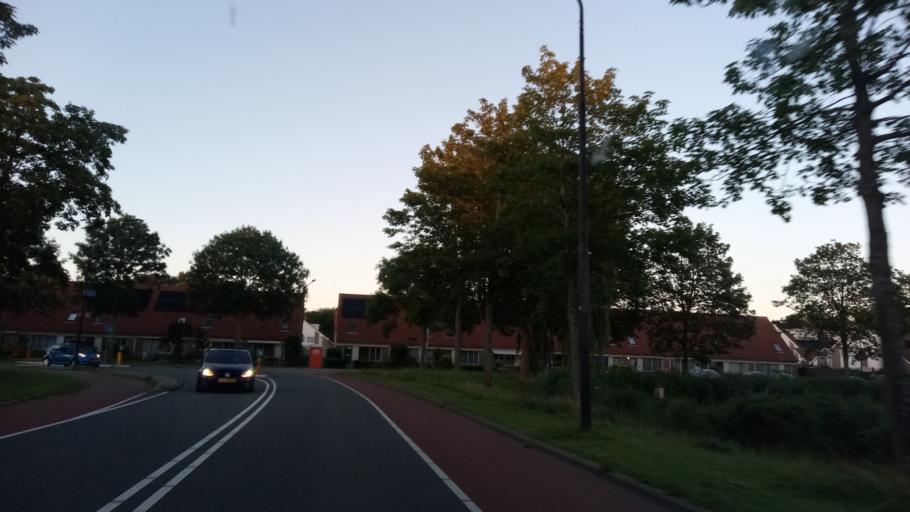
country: NL
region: North Holland
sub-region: Gemeente Langedijk
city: Broek op Langedijk
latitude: 52.6580
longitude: 4.8113
